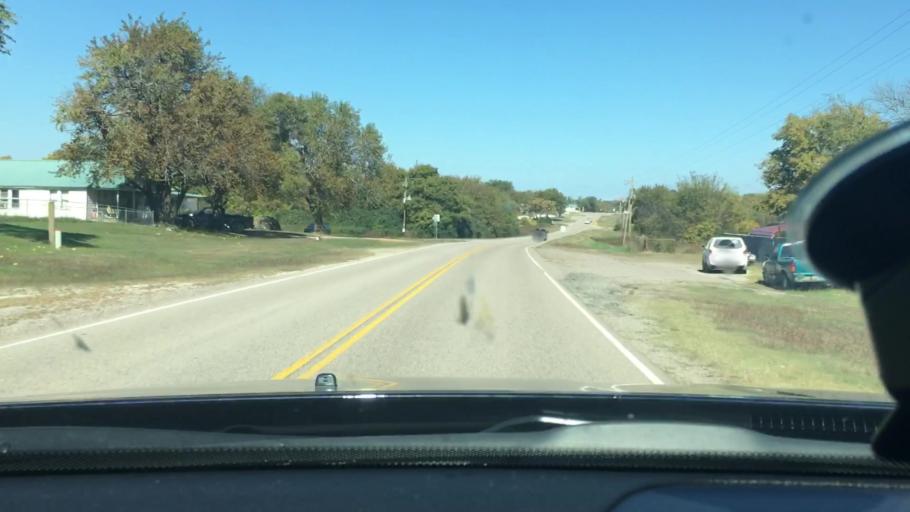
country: US
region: Oklahoma
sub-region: Johnston County
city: Tishomingo
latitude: 34.4443
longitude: -96.6361
